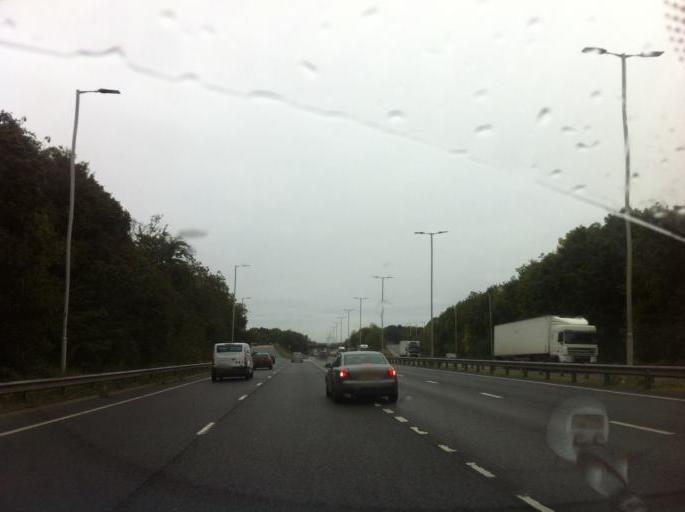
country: GB
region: England
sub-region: Cambridgeshire
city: Yaxley
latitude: 52.5447
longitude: -0.2717
